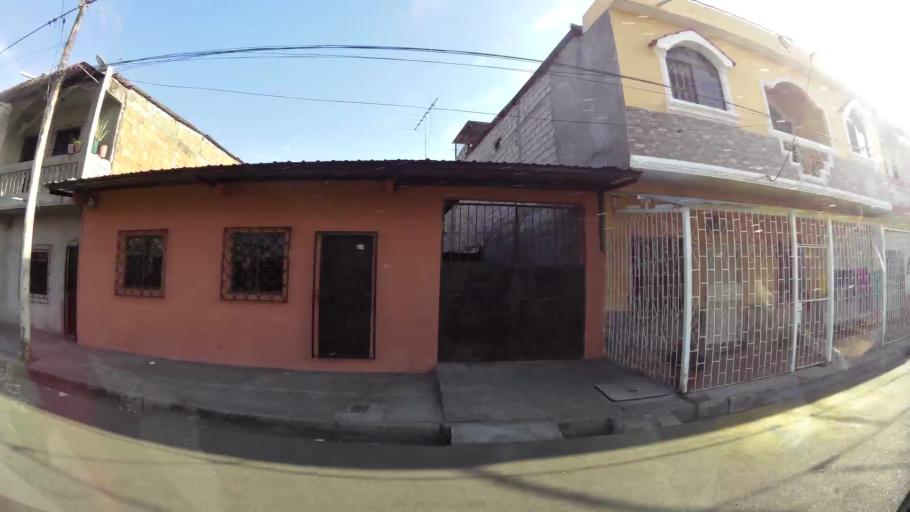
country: EC
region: Guayas
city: Guayaquil
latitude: -2.2196
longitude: -79.9188
